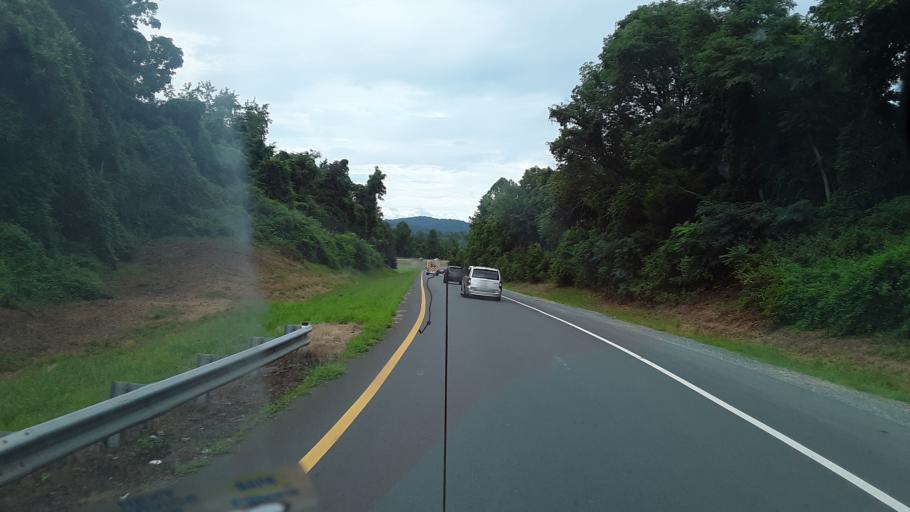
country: US
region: Virginia
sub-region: City of Charlottesville
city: Charlottesville
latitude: 38.0089
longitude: -78.5086
